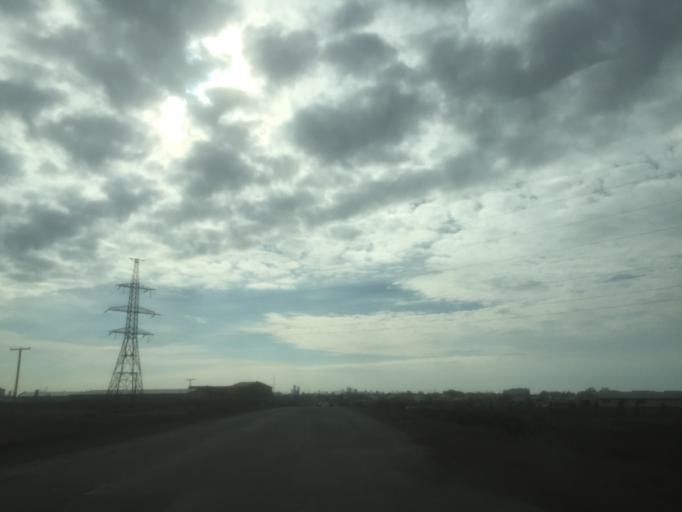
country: KZ
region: Astana Qalasy
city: Astana
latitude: 51.2237
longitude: 71.3877
